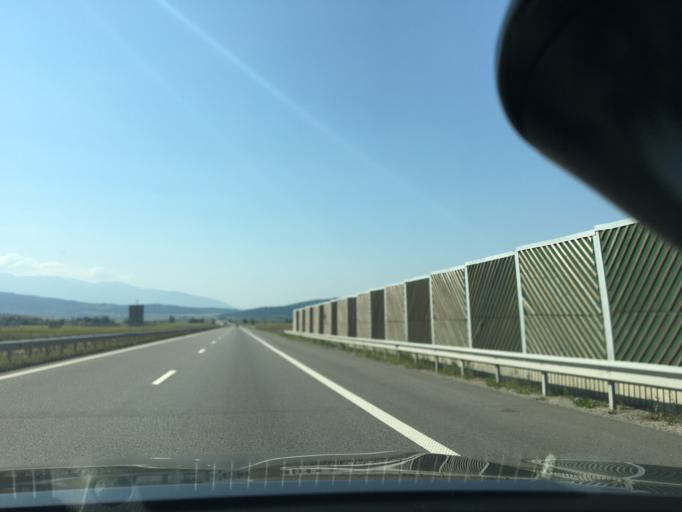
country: BG
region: Kyustendil
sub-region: Obshtina Bobovdol
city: Bobovdol
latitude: 42.4494
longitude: 23.1117
